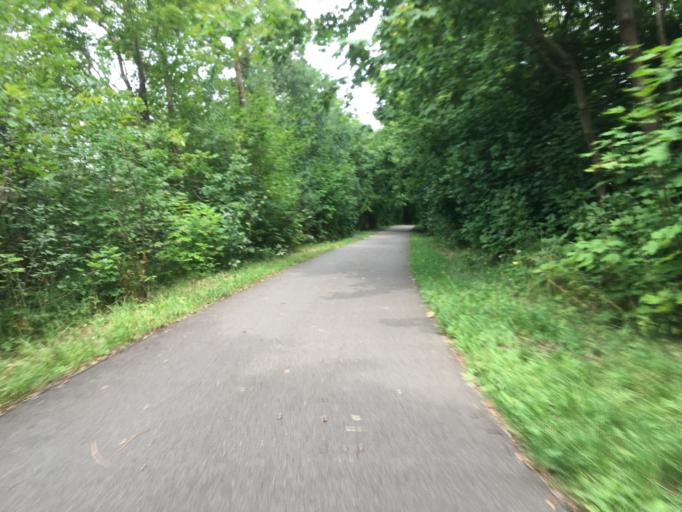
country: DE
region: Brandenburg
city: Prenzlau
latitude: 53.3009
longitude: 13.8452
